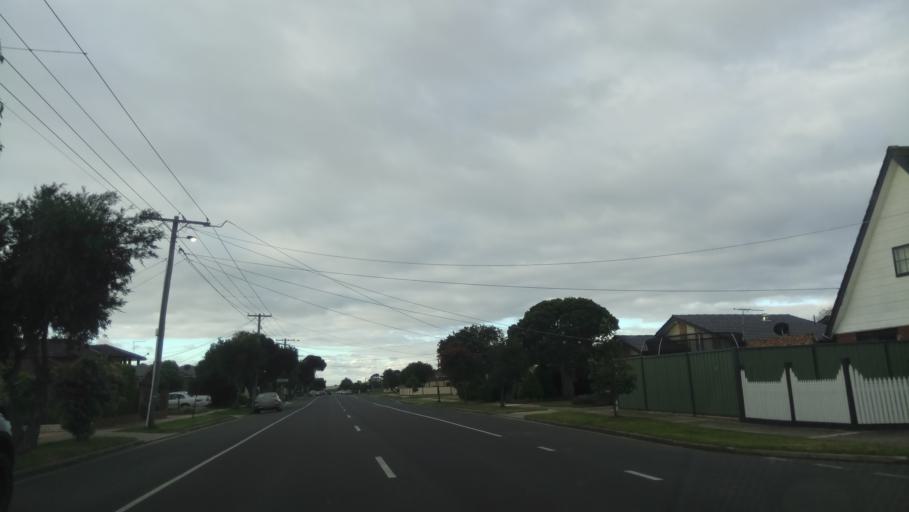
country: AU
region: Victoria
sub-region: Hobsons Bay
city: Altona Meadows
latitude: -37.8714
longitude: 144.7869
